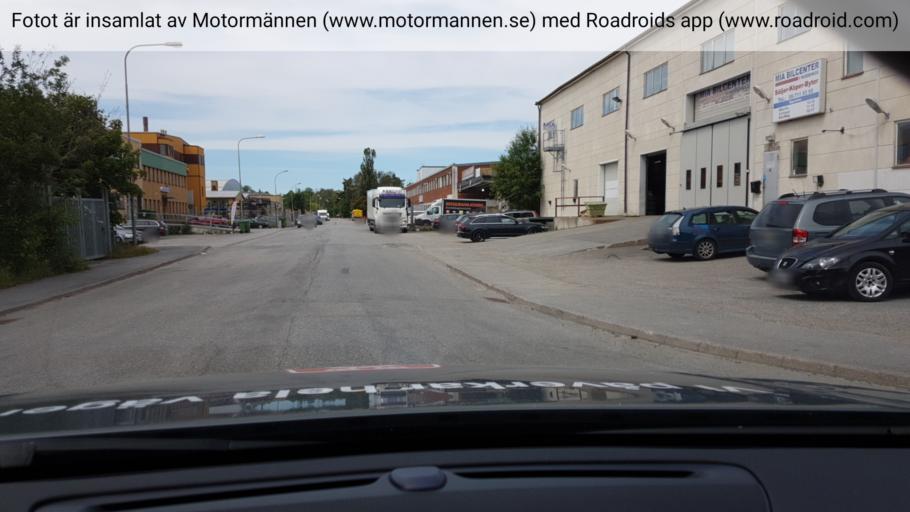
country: SE
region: Stockholm
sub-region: Huddinge Kommun
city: Huddinge
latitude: 59.2310
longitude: 17.9895
